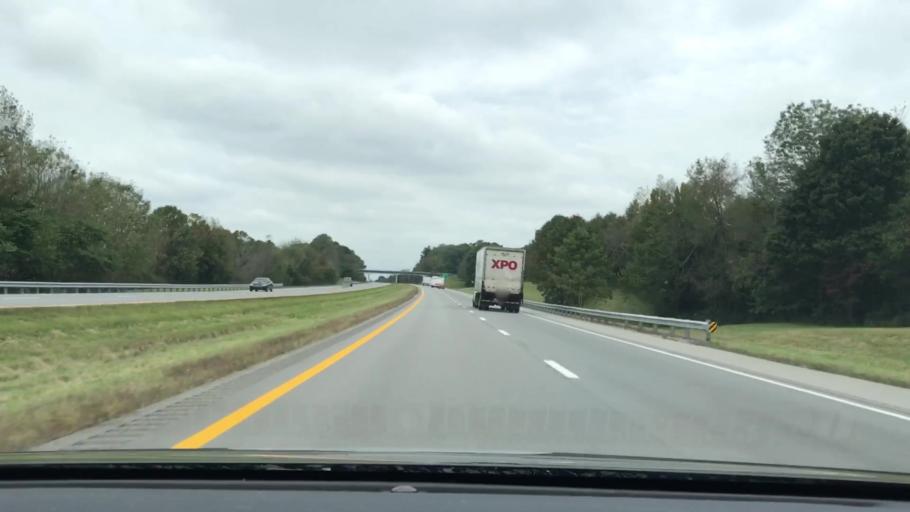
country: US
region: Kentucky
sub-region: Adair County
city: Columbia
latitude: 37.0856
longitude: -85.2600
